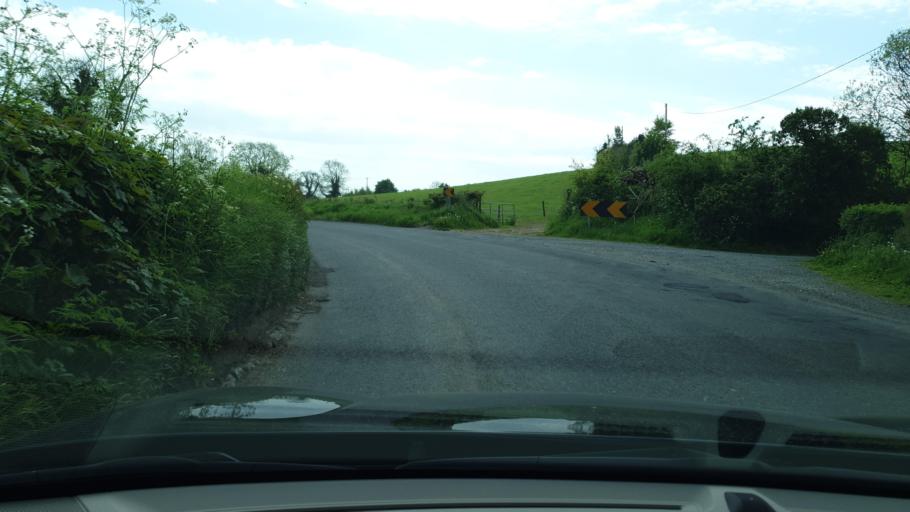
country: IE
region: Ulster
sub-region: An Cabhan
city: Kingscourt
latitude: 53.8311
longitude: -6.7613
